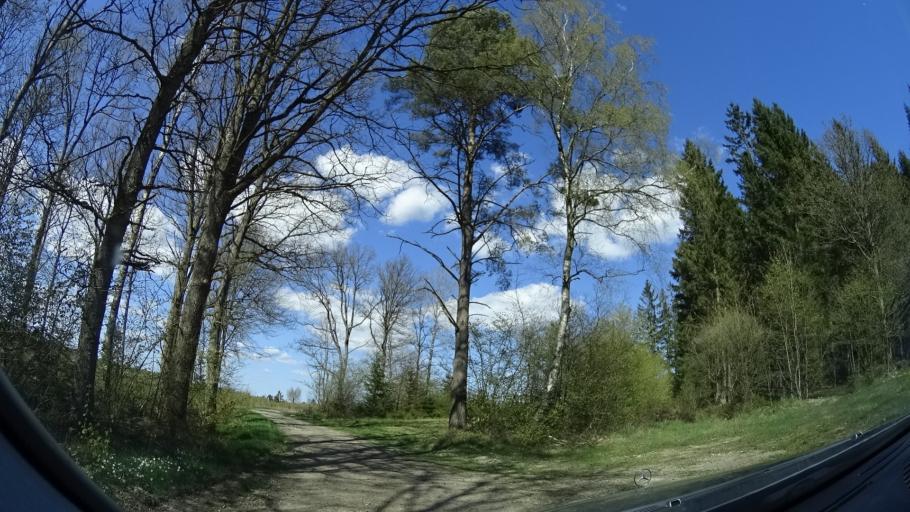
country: SE
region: Skane
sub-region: Hassleholms Kommun
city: Tormestorp
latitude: 56.0880
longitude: 13.6921
